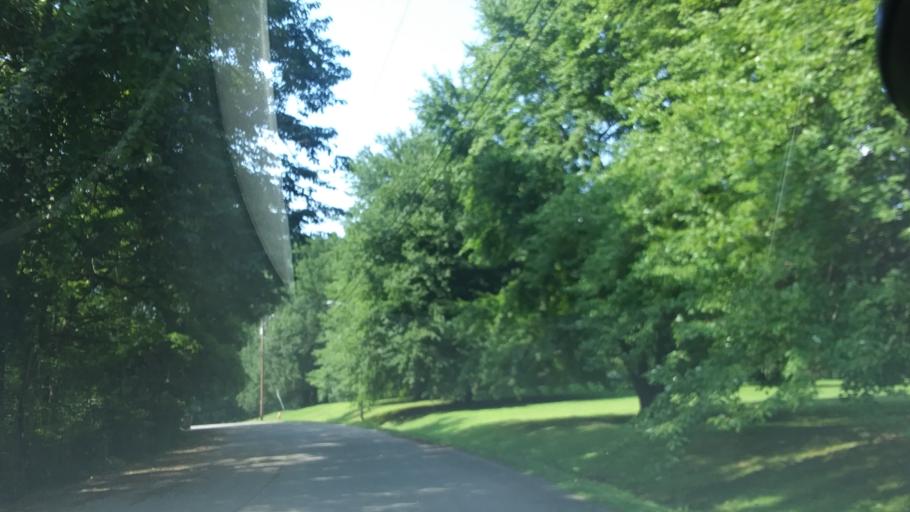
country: US
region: Tennessee
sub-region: Rutherford County
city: La Vergne
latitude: 36.0986
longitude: -86.6405
